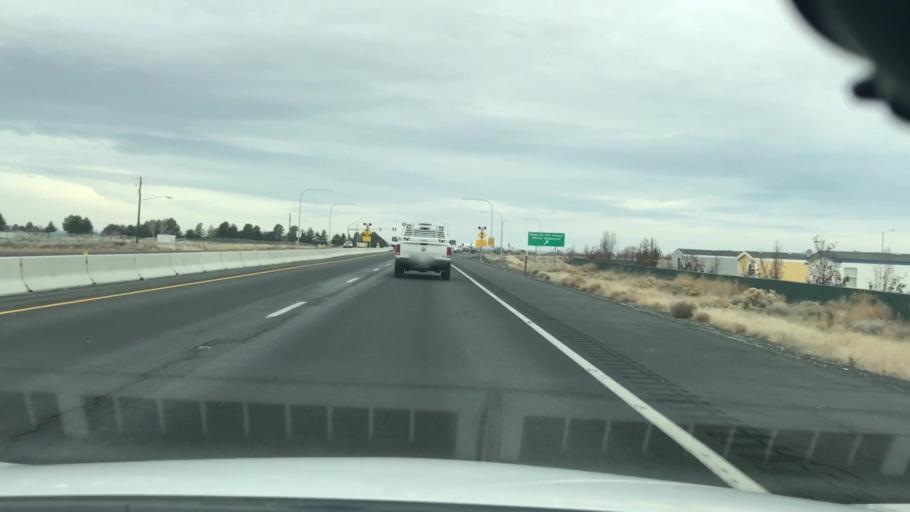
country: US
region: Washington
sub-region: Grant County
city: Cascade Valley
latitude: 47.1555
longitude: -119.3086
